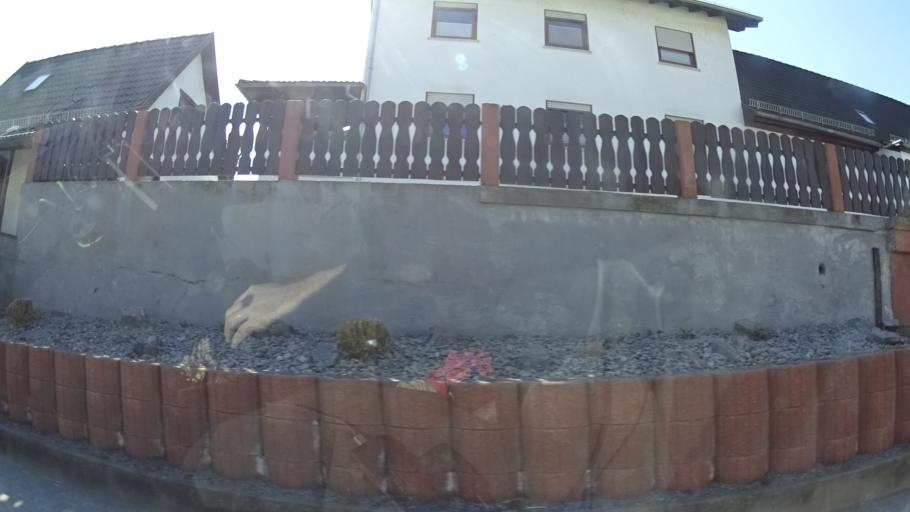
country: DE
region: Hesse
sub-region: Regierungsbezirk Darmstadt
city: Wald-Michelbach
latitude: 49.5866
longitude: 8.8145
